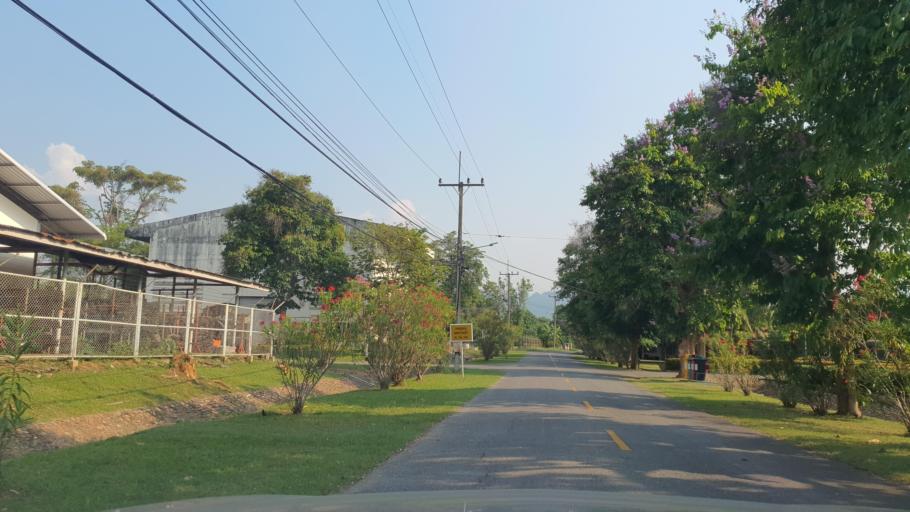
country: TH
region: Kanchanaburi
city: Sai Yok
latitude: 14.2283
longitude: 99.2349
